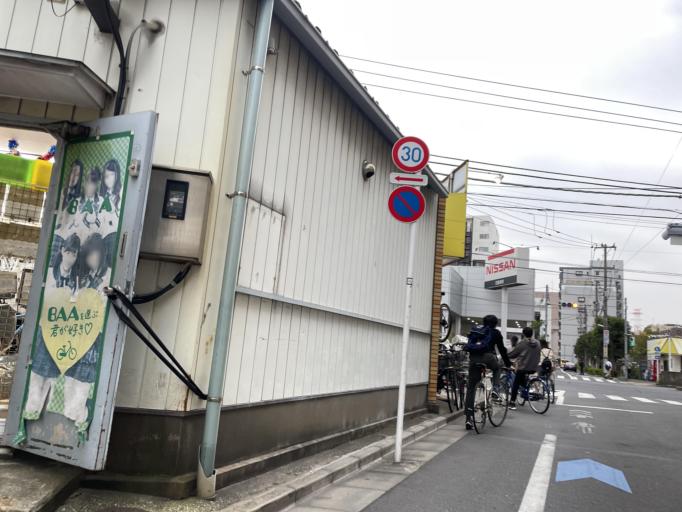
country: JP
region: Tokyo
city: Urayasu
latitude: 35.6698
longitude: 139.8615
